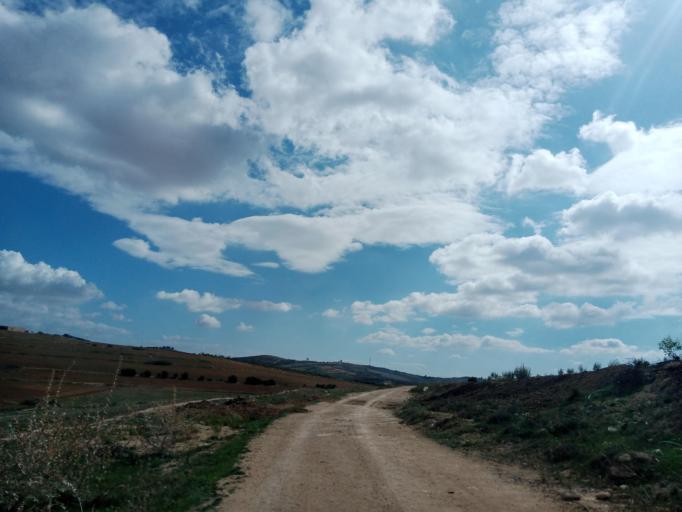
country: TN
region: Tunis
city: Oued Lill
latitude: 36.8093
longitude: 9.9833
